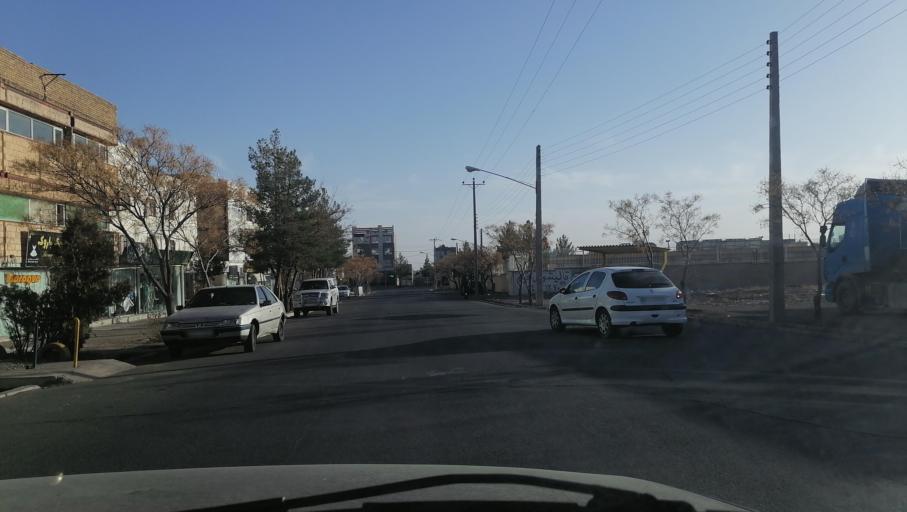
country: IR
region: Razavi Khorasan
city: Sabzevar
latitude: 36.2869
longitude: 57.6765
